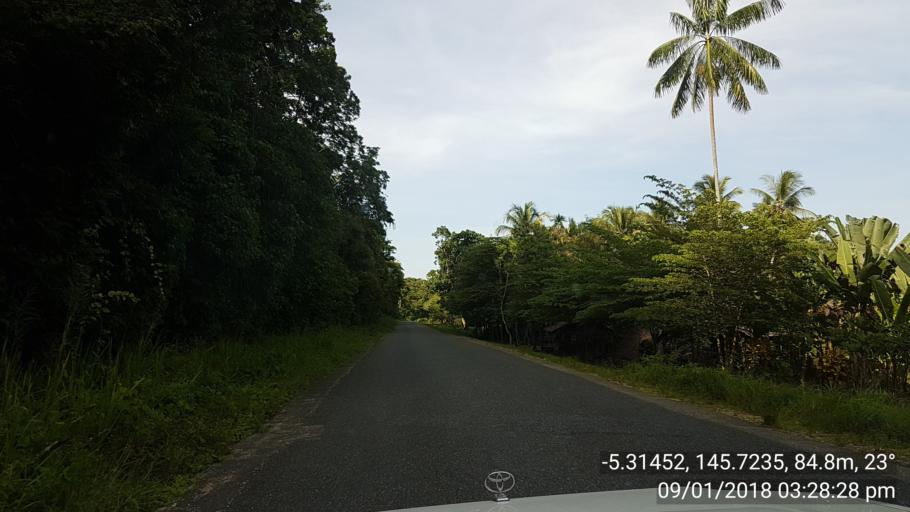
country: PG
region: Madang
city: Madang
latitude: -5.3147
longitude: 145.7236
